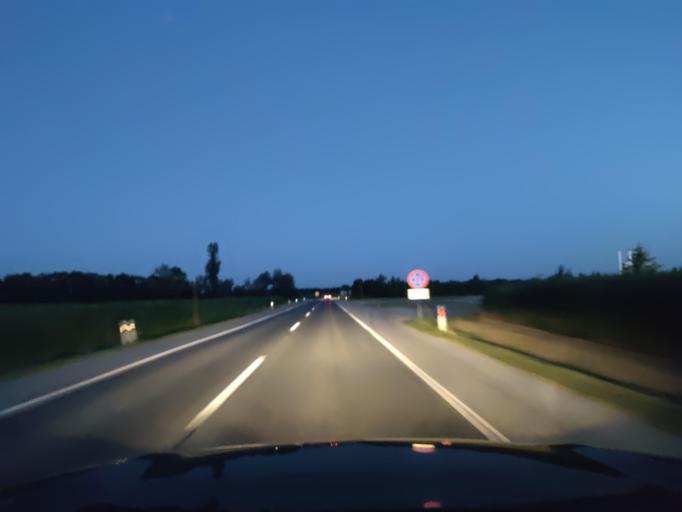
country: HR
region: Medimurska
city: Mackovec
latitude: 46.4369
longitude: 16.4308
